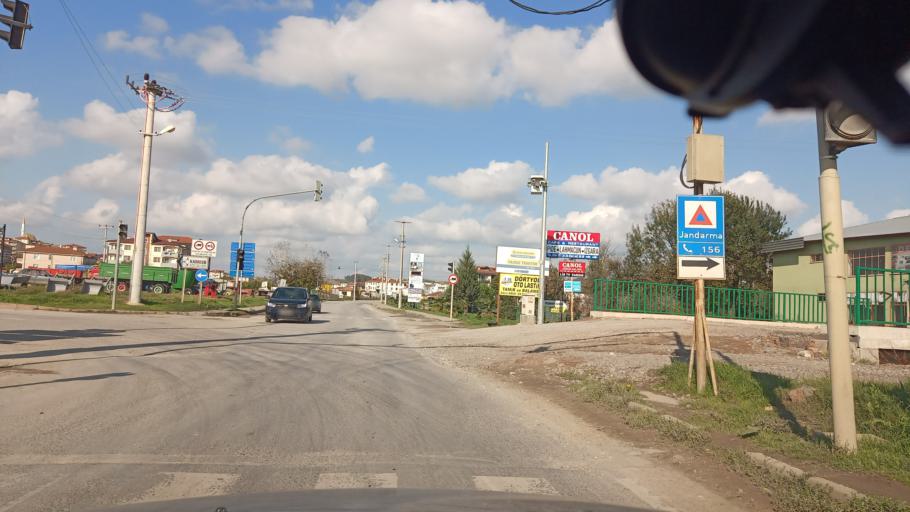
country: TR
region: Sakarya
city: Kaynarca
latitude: 41.0282
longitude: 30.3074
